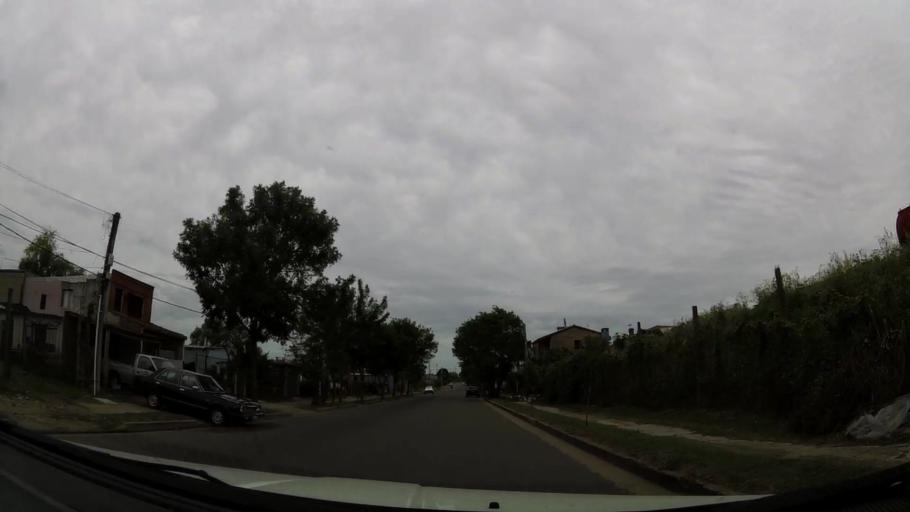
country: UY
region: Maldonado
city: Maldonado
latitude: -34.8900
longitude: -54.9406
